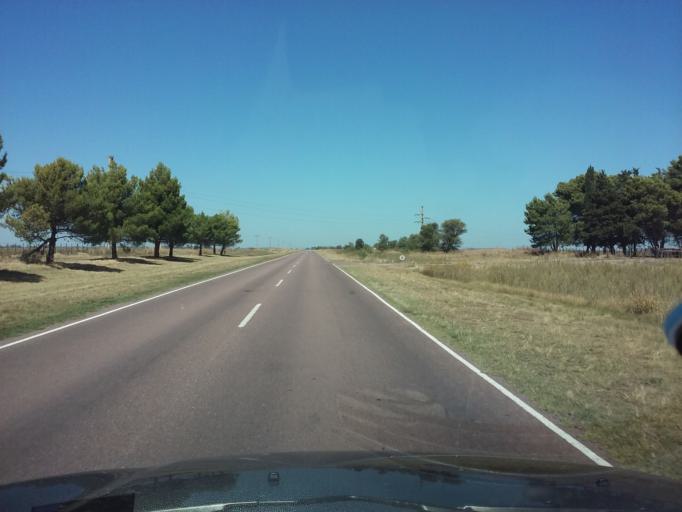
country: AR
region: La Pampa
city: Colonia Baron
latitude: -36.0369
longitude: -63.9414
